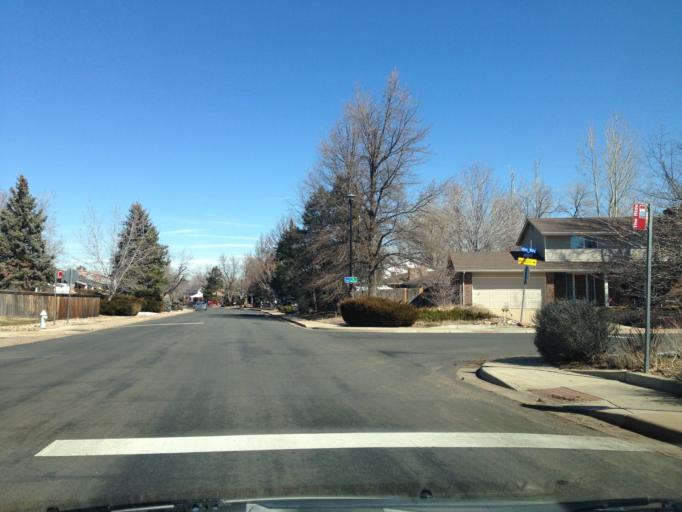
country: US
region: Colorado
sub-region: Boulder County
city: Boulder
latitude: 39.9878
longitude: -105.2275
